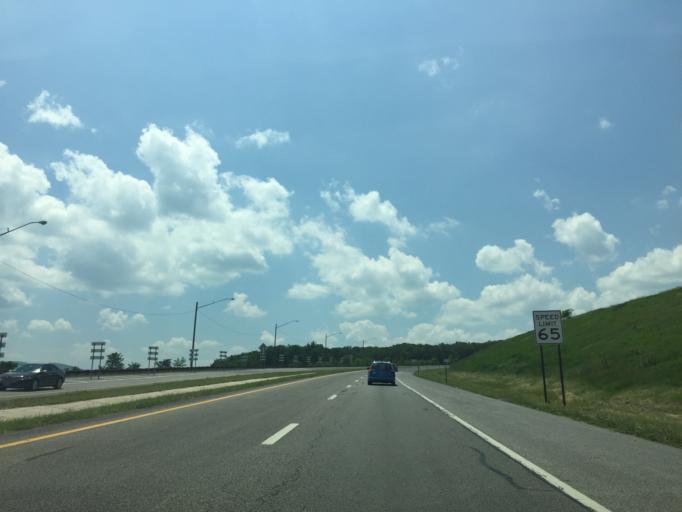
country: US
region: Virginia
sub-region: Shenandoah County
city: Woodstock
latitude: 39.0727
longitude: -78.6293
